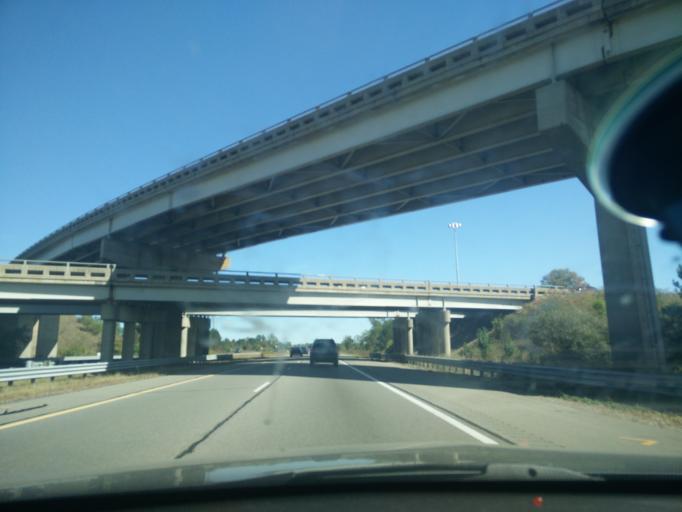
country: US
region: Michigan
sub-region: Oakland County
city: Novi
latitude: 42.4845
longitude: -83.4326
